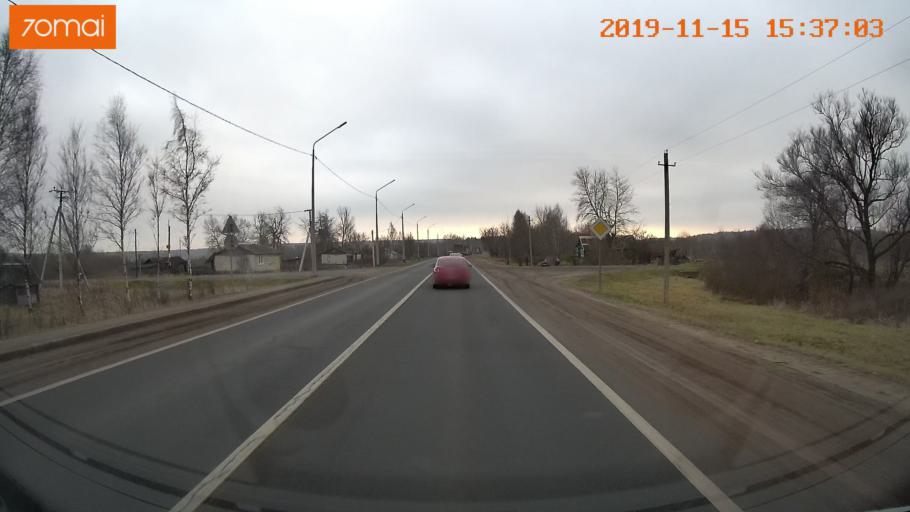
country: RU
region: Jaroslavl
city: Danilov
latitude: 58.0432
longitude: 40.0909
